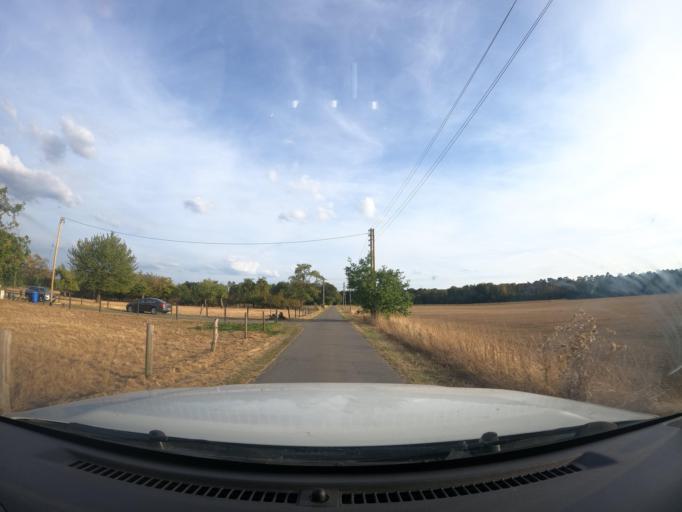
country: DE
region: North Rhine-Westphalia
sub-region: Regierungsbezirk Dusseldorf
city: Hamminkeln
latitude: 51.7046
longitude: 6.5691
